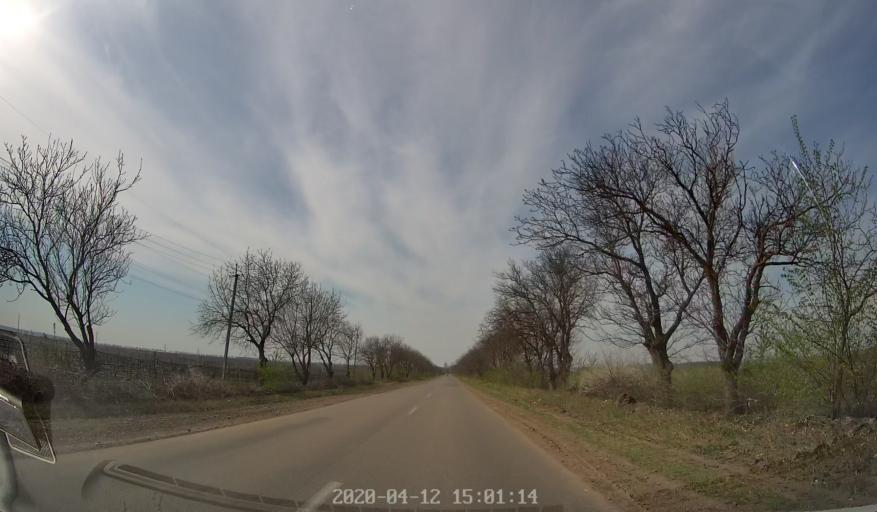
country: MD
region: Telenesti
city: Cocieri
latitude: 47.2842
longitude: 29.0894
